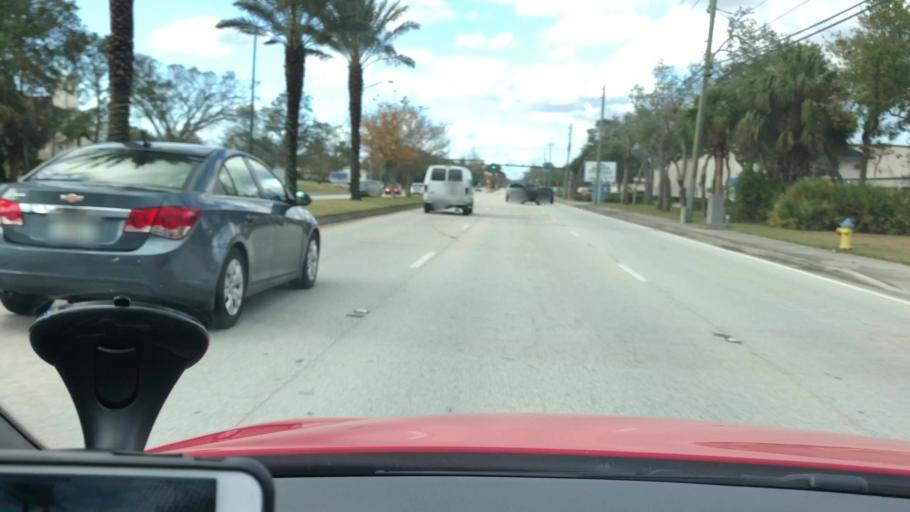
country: US
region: Florida
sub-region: Volusia County
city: Ormond Beach
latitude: 29.2652
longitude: -81.0779
